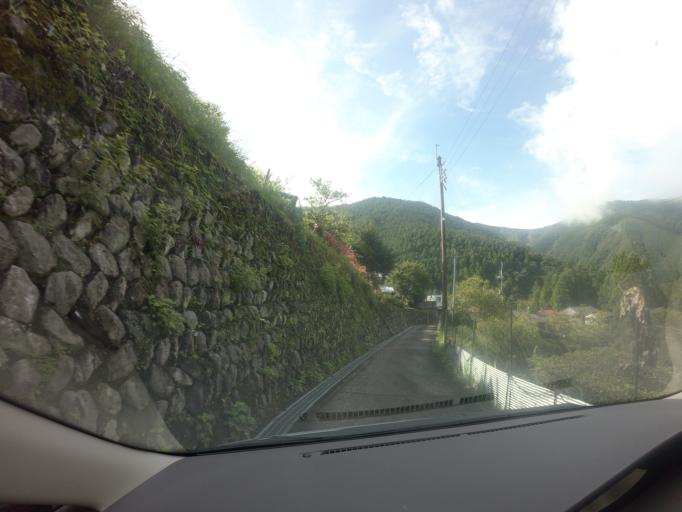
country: JP
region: Wakayama
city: Shingu
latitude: 33.9685
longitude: 135.8428
